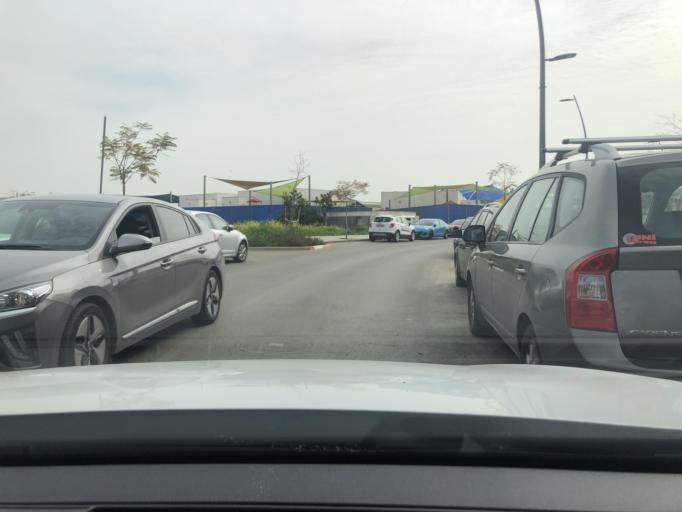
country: IL
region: Central District
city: Rosh Ha'Ayin
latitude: 32.1069
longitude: 34.9483
